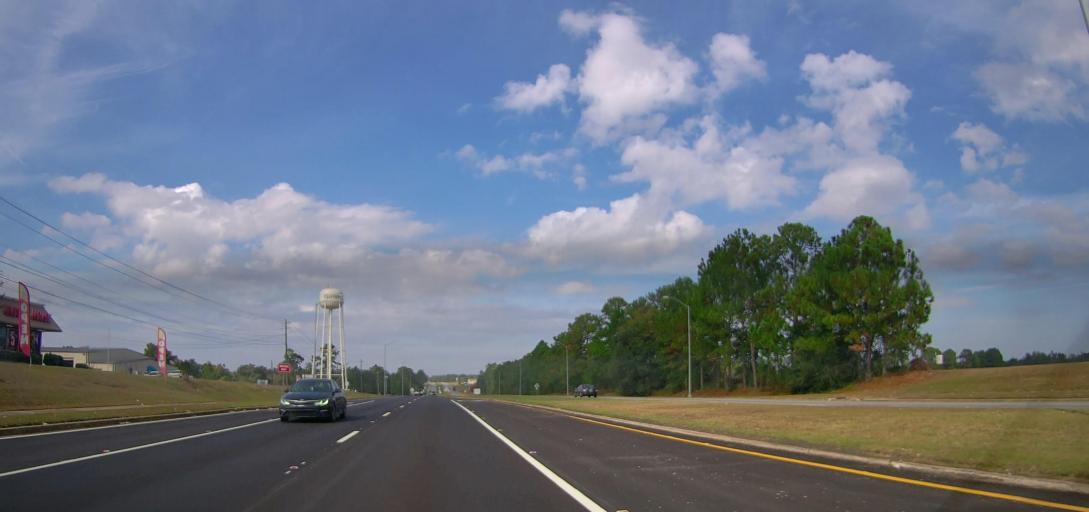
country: US
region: Georgia
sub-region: Mitchell County
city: Pelham
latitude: 31.1358
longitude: -84.1406
